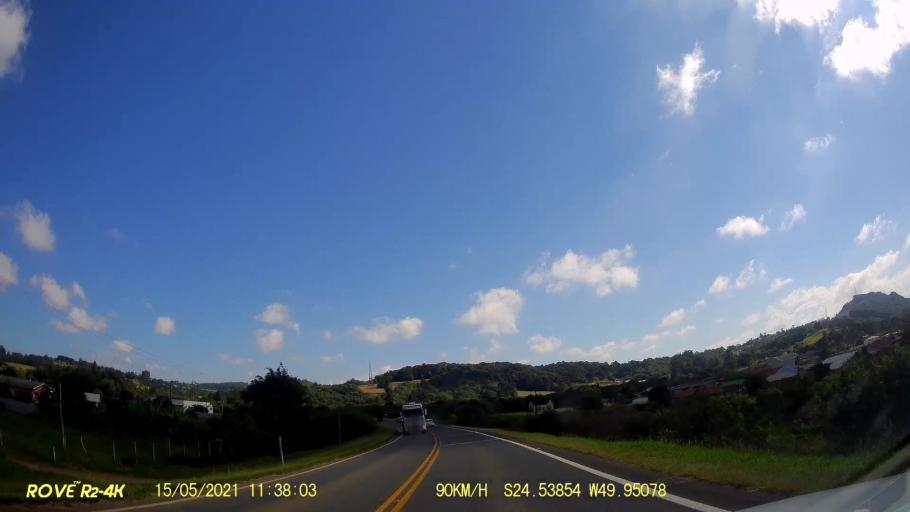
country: BR
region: Parana
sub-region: Pirai Do Sul
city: Pirai do Sul
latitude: -24.5399
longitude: -49.9496
